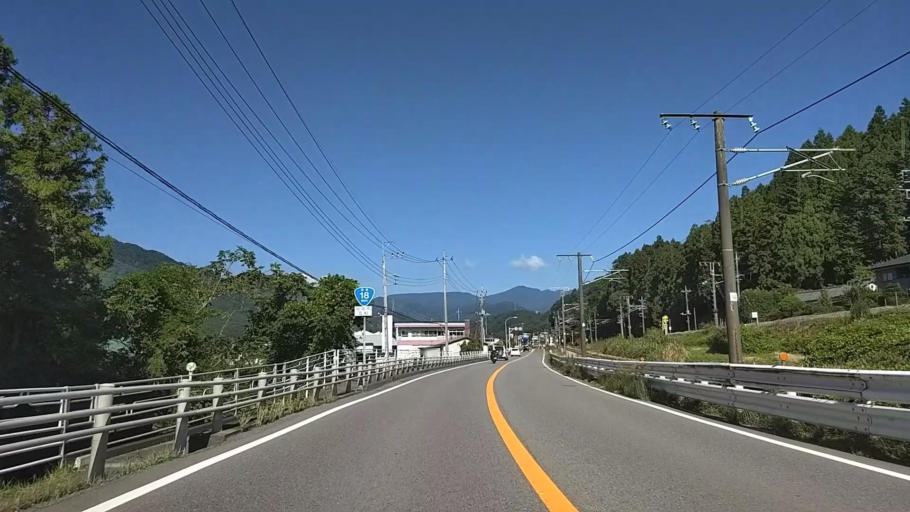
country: JP
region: Gunma
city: Annaka
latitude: 36.3260
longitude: 138.7587
